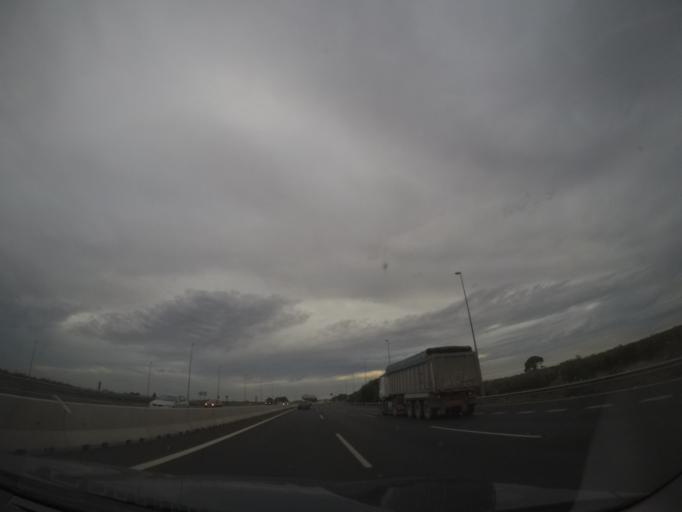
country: ES
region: Andalusia
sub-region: Provincia de Sevilla
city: Umbrete
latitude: 37.3571
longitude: -6.1741
